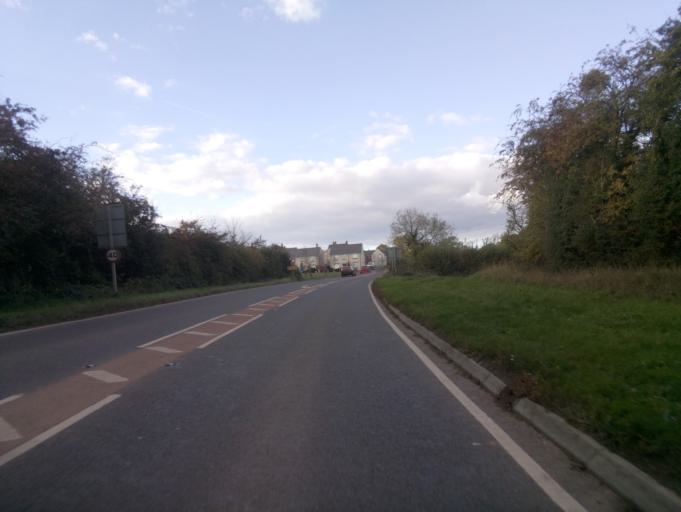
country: GB
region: England
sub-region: Herefordshire
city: Withington
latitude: 52.0643
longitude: -2.6307
